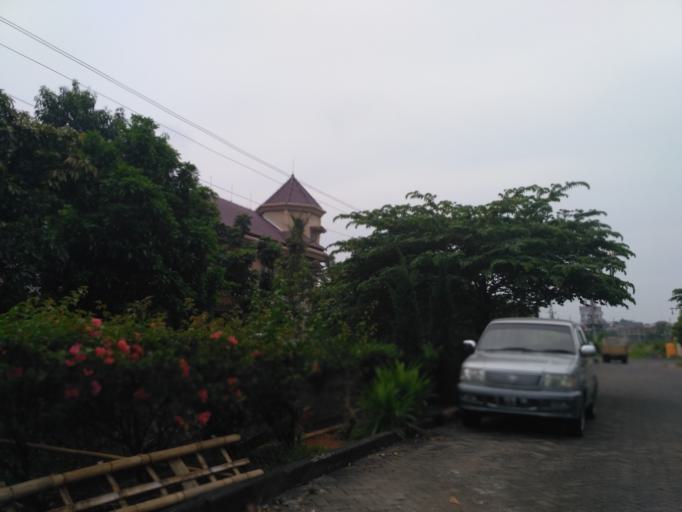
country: ID
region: Central Java
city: Semarang
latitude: -7.0624
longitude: 110.4313
